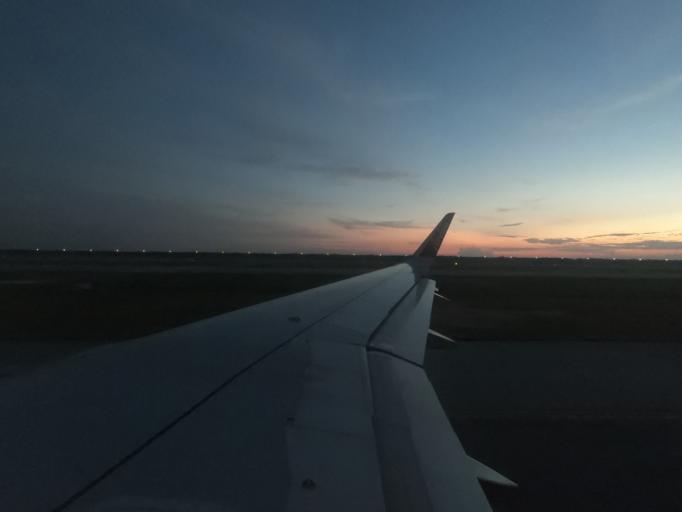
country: MY
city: Sungai Pelek New Village
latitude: 2.7241
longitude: 101.6903
